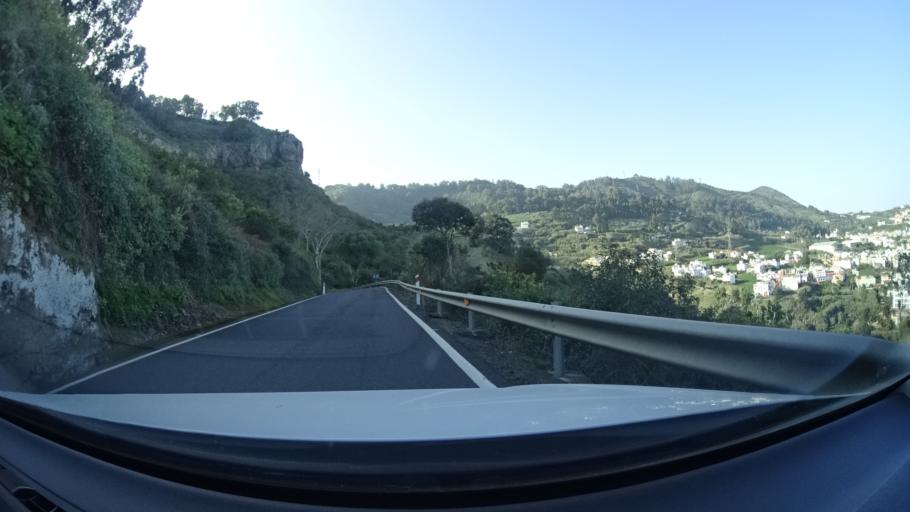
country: ES
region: Canary Islands
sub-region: Provincia de Las Palmas
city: Teror
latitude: 28.0551
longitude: -15.5550
